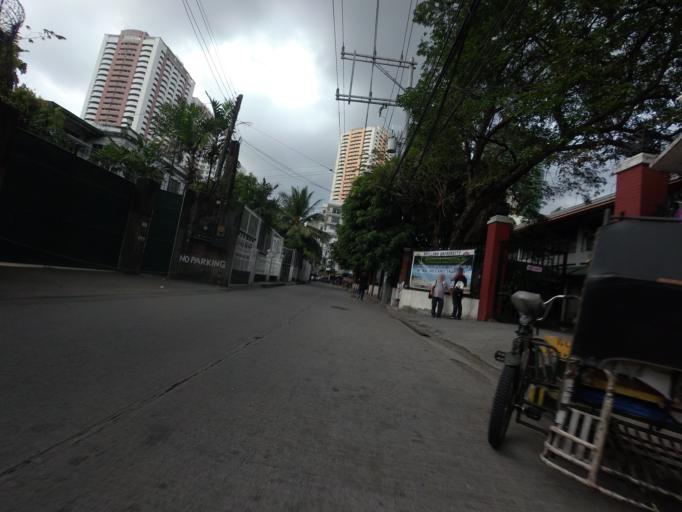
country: PH
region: Metro Manila
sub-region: City of Manila
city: Port Area
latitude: 14.5594
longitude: 120.9947
